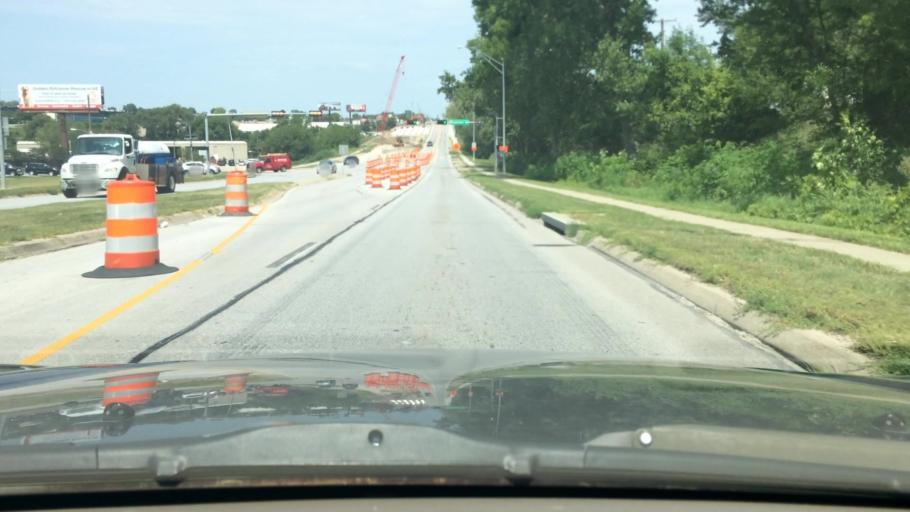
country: US
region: Nebraska
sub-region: Douglas County
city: Ralston
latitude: 41.1948
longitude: -96.0429
